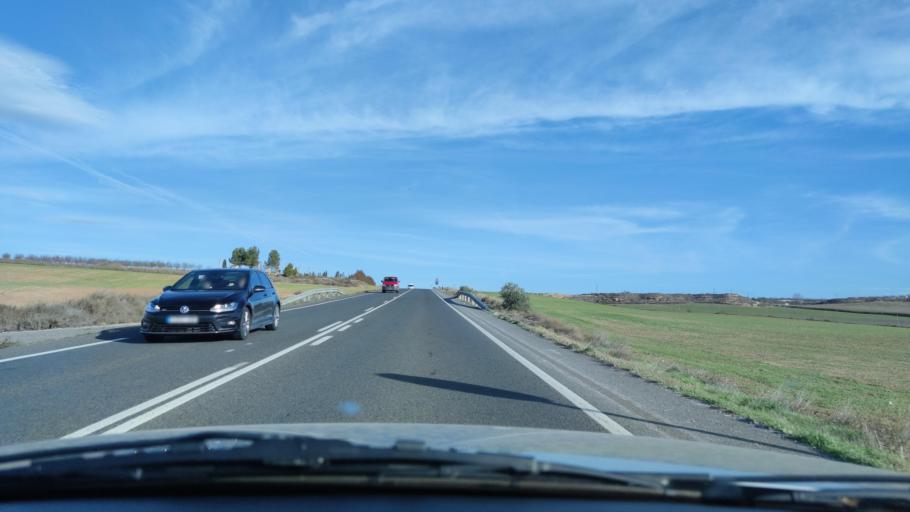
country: ES
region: Catalonia
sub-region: Provincia de Lleida
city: Alfes
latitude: 41.5057
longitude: 0.6191
